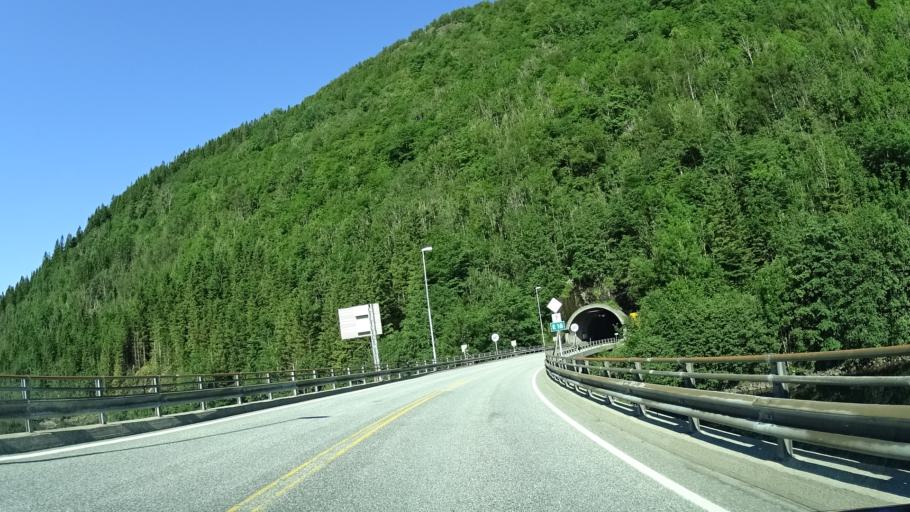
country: NO
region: Hordaland
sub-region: Samnanger
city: Tysse
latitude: 60.3791
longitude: 5.7857
